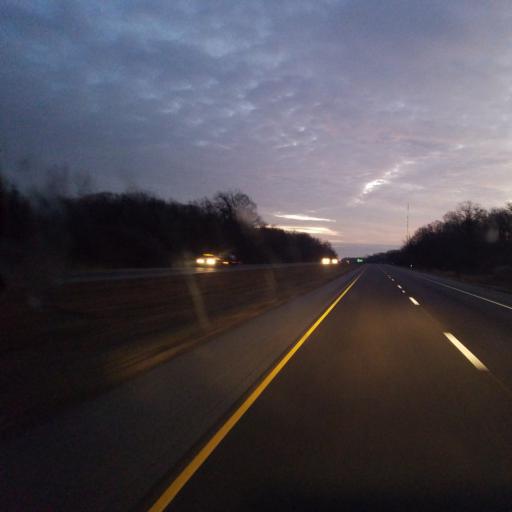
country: US
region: Illinois
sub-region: Tazewell County
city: Creve Coeur
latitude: 40.6303
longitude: -89.5667
